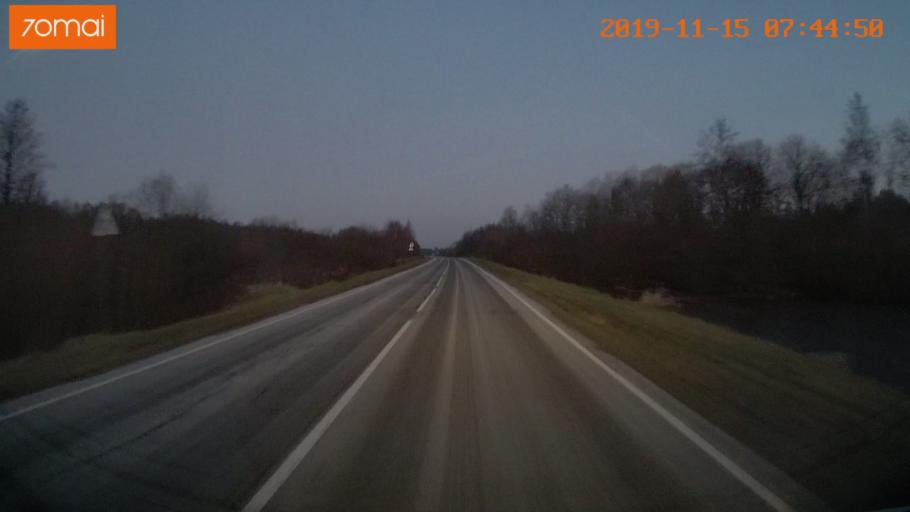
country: RU
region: Vologda
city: Sheksna
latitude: 58.8179
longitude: 38.3069
